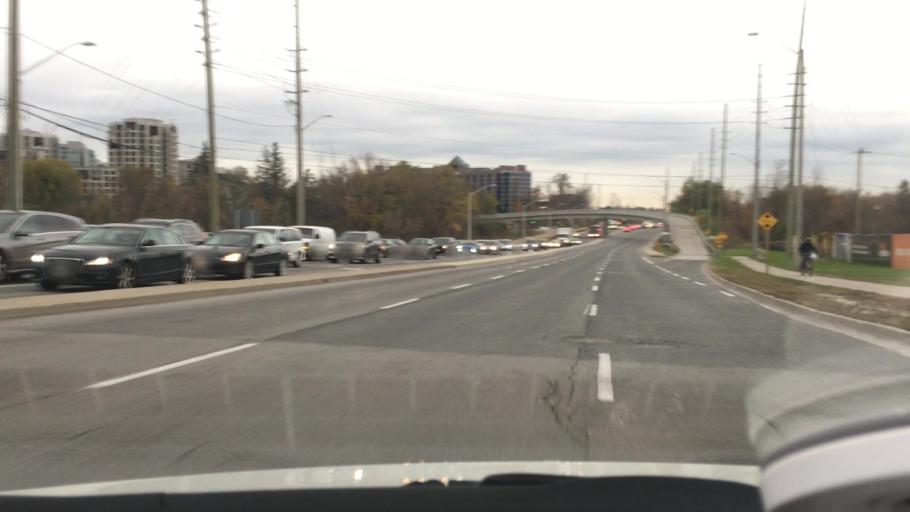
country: CA
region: Ontario
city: Markham
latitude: 43.8489
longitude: -79.3320
